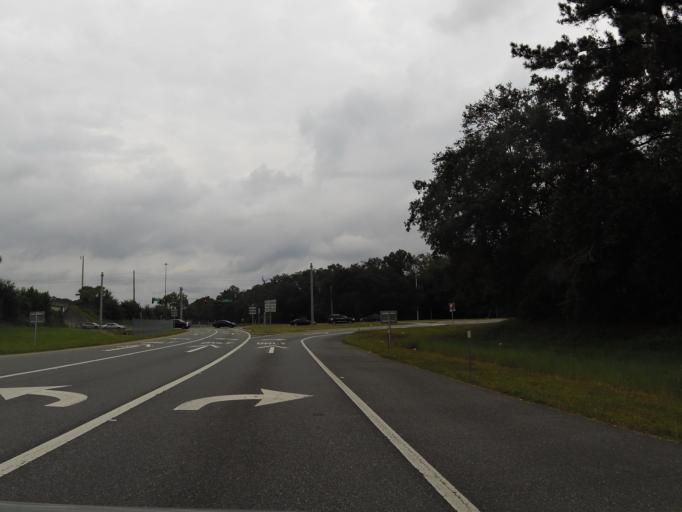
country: US
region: Florida
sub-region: Clay County
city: Bellair-Meadowbrook Terrace
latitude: 30.2690
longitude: -81.7663
